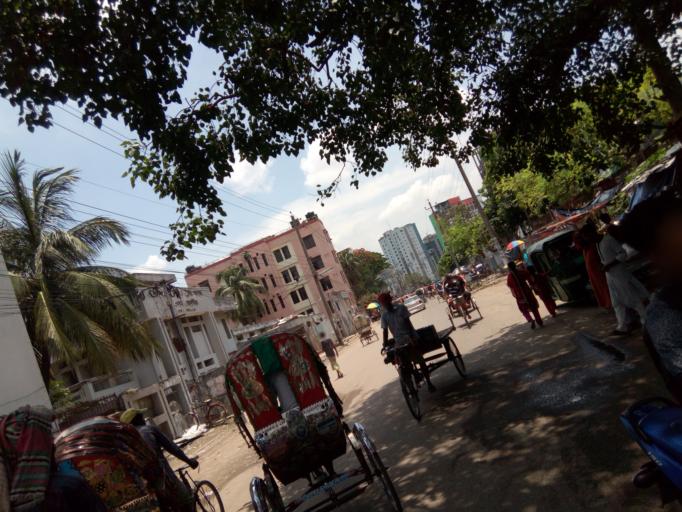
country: BD
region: Dhaka
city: Paltan
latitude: 23.7582
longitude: 90.4012
